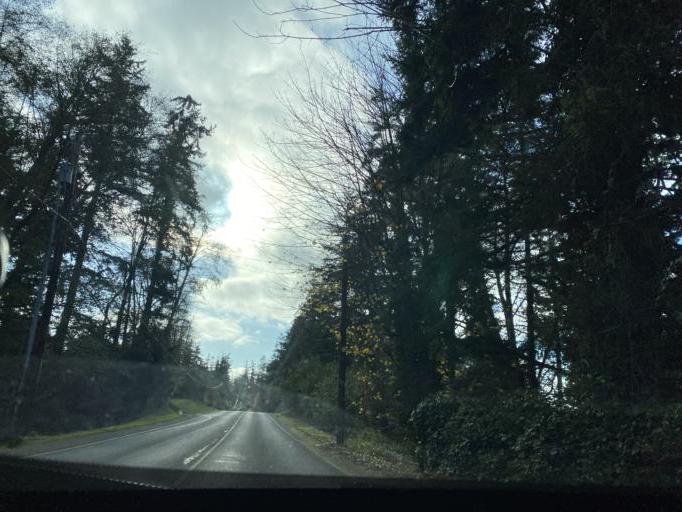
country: US
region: Washington
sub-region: Island County
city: Freeland
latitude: 47.9825
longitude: -122.4618
